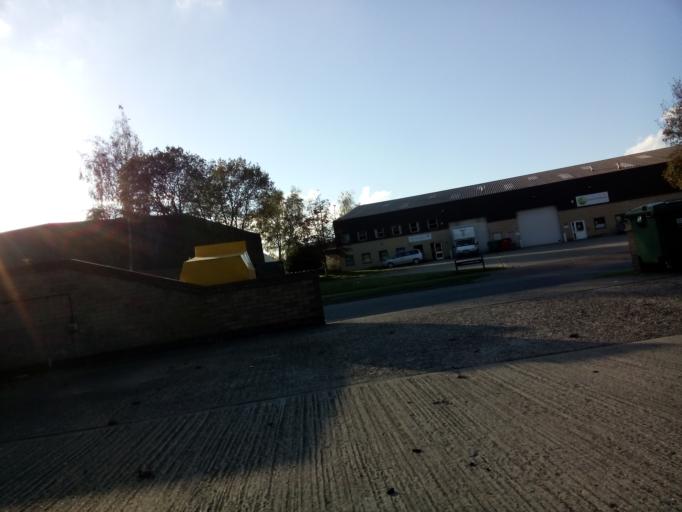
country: GB
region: England
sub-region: Suffolk
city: Kesgrave
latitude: 52.0633
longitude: 1.2811
